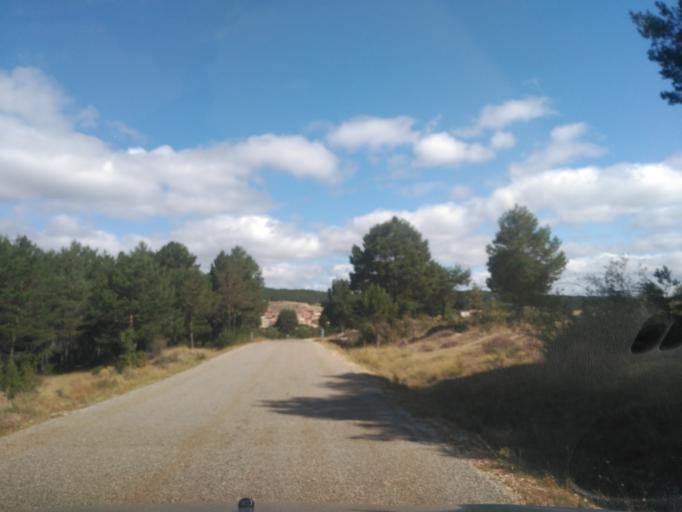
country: ES
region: Castille and Leon
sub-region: Provincia de Soria
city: Espejon
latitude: 41.8477
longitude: -3.2305
